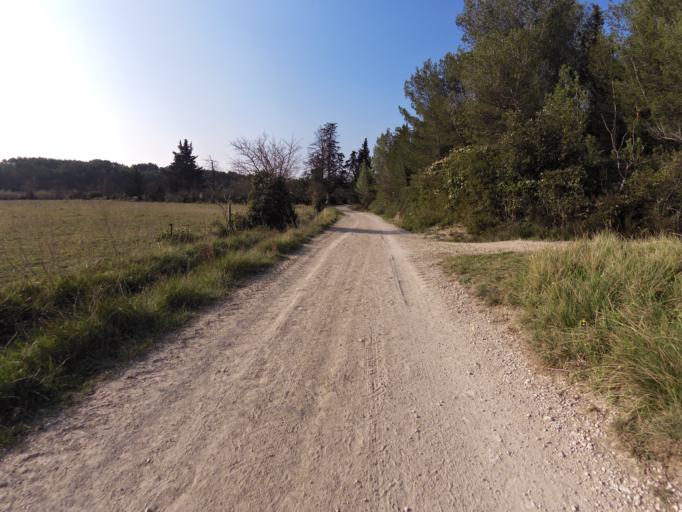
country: FR
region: Languedoc-Roussillon
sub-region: Departement du Gard
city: Gallargues-le-Montueux
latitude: 43.7352
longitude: 4.1598
